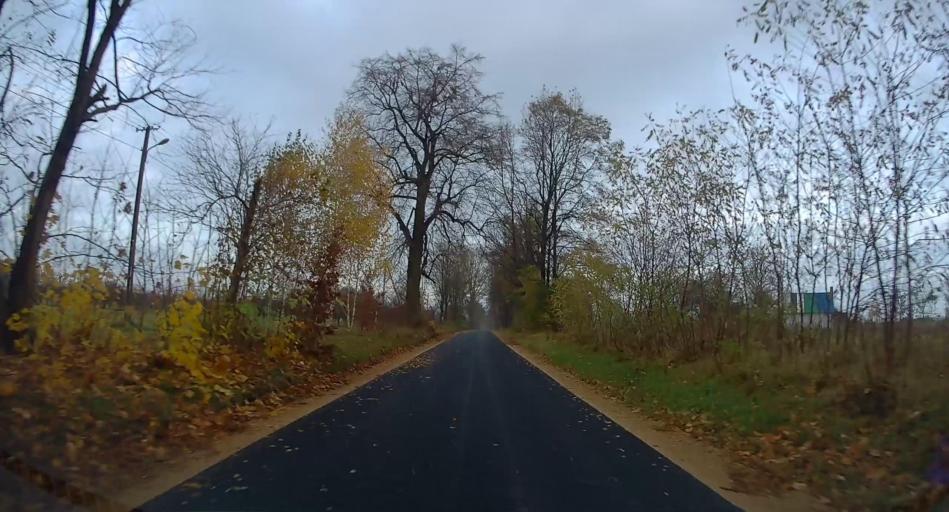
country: PL
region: Lodz Voivodeship
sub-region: Powiat skierniewicki
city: Kowiesy
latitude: 51.9231
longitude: 20.4108
